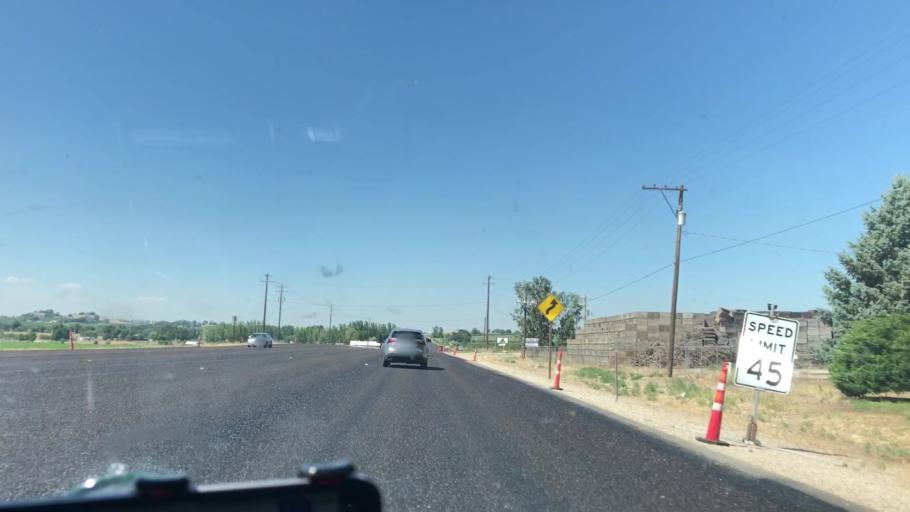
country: US
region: Idaho
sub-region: Owyhee County
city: Marsing
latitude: 43.5762
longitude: -116.7924
